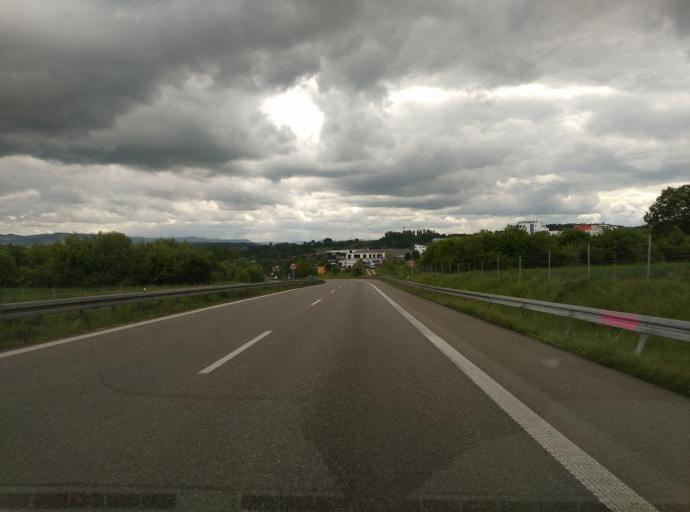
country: DE
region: Baden-Wuerttemberg
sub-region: Regierungsbezirk Stuttgart
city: Nurtingen
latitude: 48.6488
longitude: 9.3340
